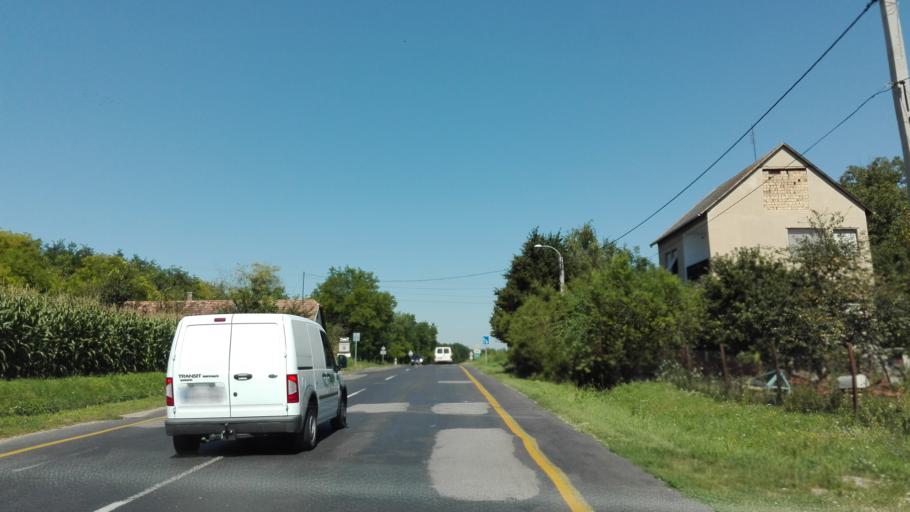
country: HU
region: Fejer
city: Mezoszilas
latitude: 46.7837
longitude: 18.5075
